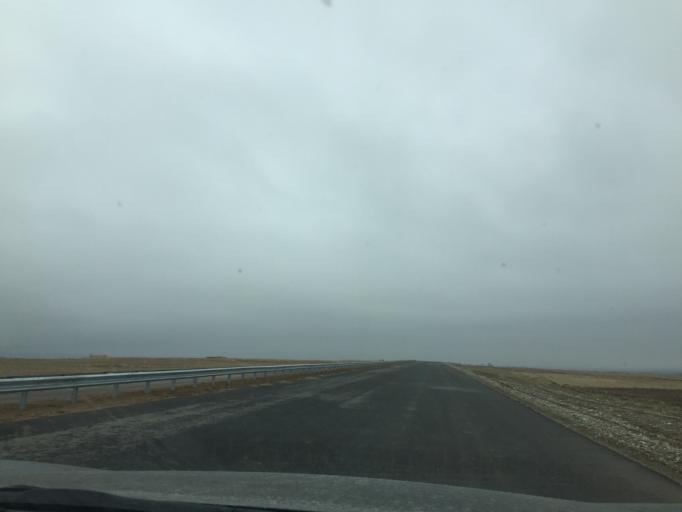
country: KZ
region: Ongtustik Qazaqstan
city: Kokterek
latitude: 42.5424
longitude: 70.2797
